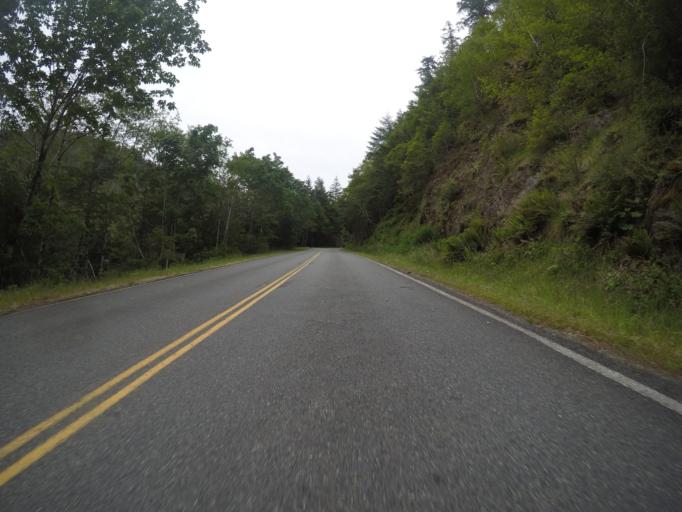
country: US
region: California
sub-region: Del Norte County
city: Bertsch-Oceanview
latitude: 41.7718
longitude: -124.0139
